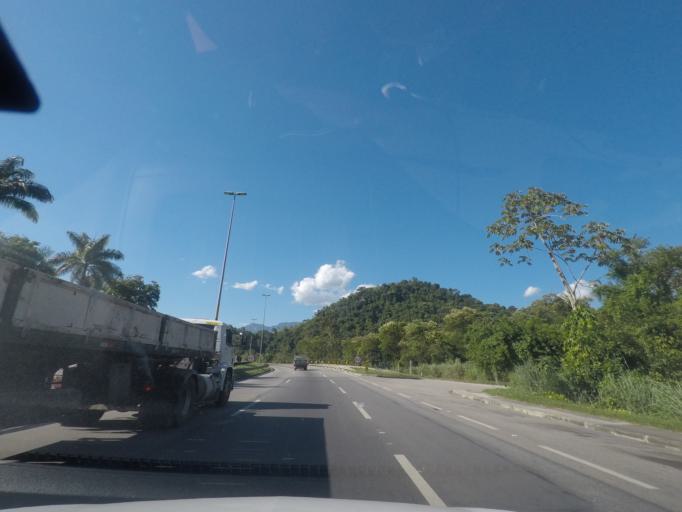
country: BR
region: Rio de Janeiro
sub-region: Petropolis
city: Petropolis
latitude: -22.6604
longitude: -43.1164
